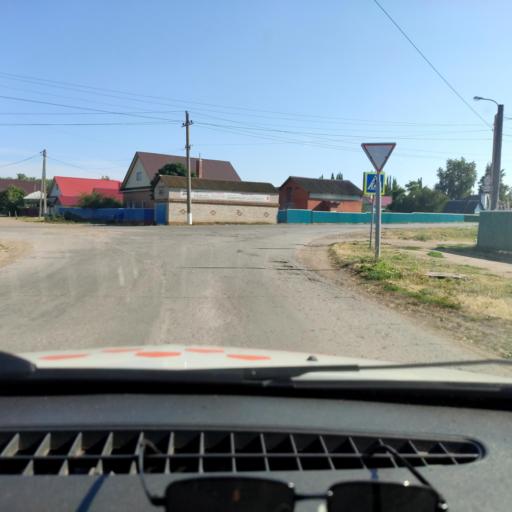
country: RU
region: Bashkortostan
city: Tolbazy
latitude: 54.0105
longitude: 55.8842
